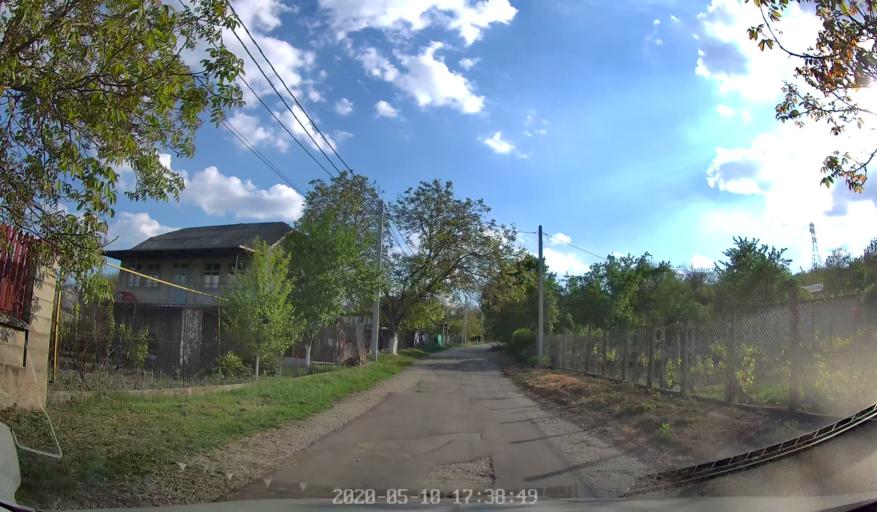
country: MD
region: Chisinau
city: Vadul lui Voda
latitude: 47.0916
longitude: 29.0709
